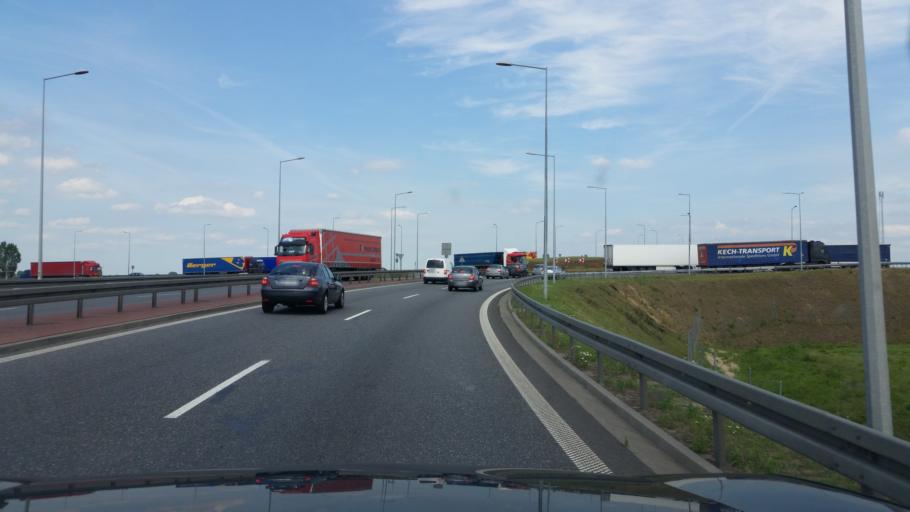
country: PL
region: Masovian Voivodeship
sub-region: Powiat zyrardowski
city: Wiskitki
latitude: 52.0908
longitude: 20.3622
